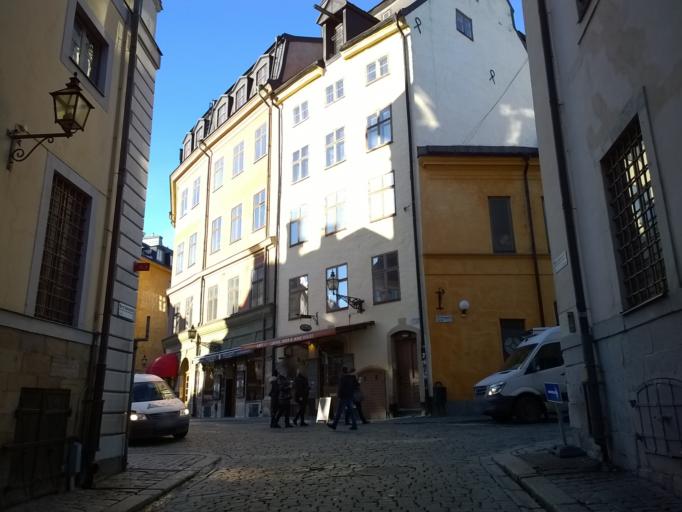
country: SE
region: Stockholm
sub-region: Stockholms Kommun
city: Stockholm
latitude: 59.3228
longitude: 18.0737
